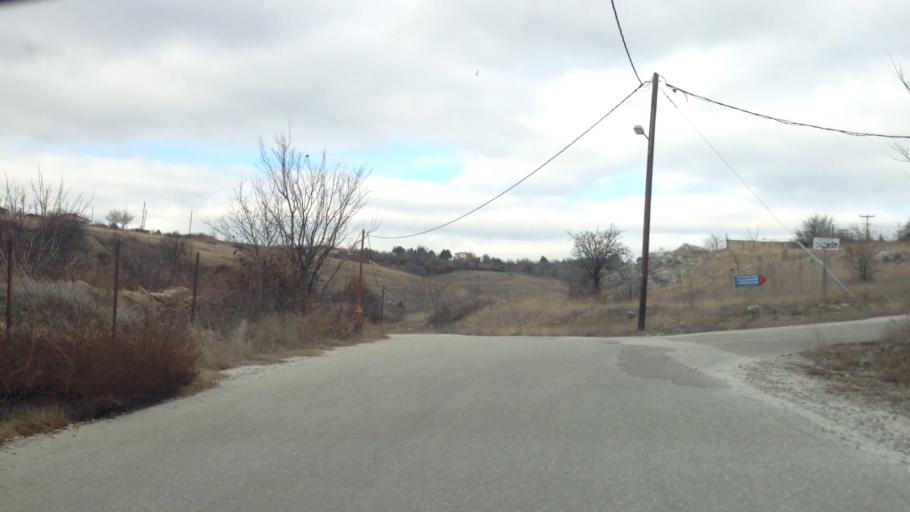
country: GR
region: West Macedonia
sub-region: Nomos Kozanis
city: Kozani
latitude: 40.2949
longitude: 21.7720
